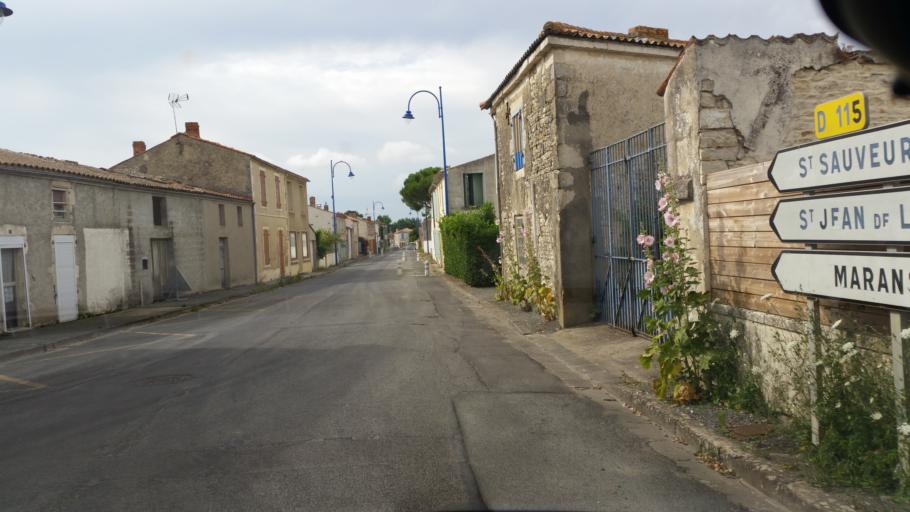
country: FR
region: Poitou-Charentes
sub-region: Departement de la Charente-Maritime
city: Courcon
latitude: 46.1855
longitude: -0.8604
